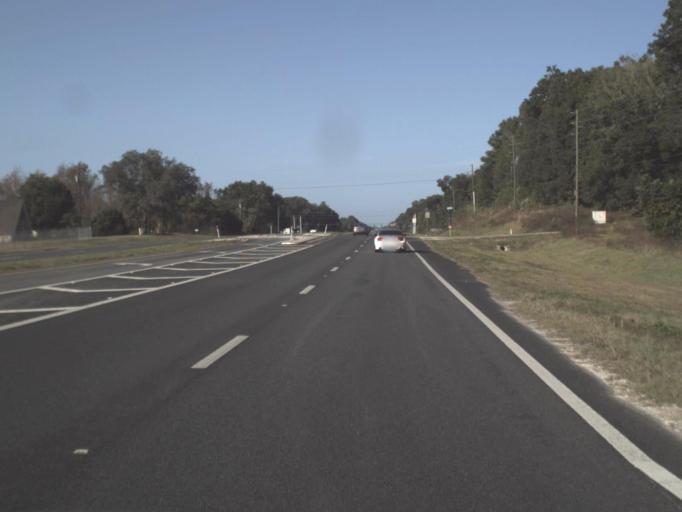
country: US
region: Florida
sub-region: Marion County
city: Belleview
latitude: 29.0261
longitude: -82.0822
